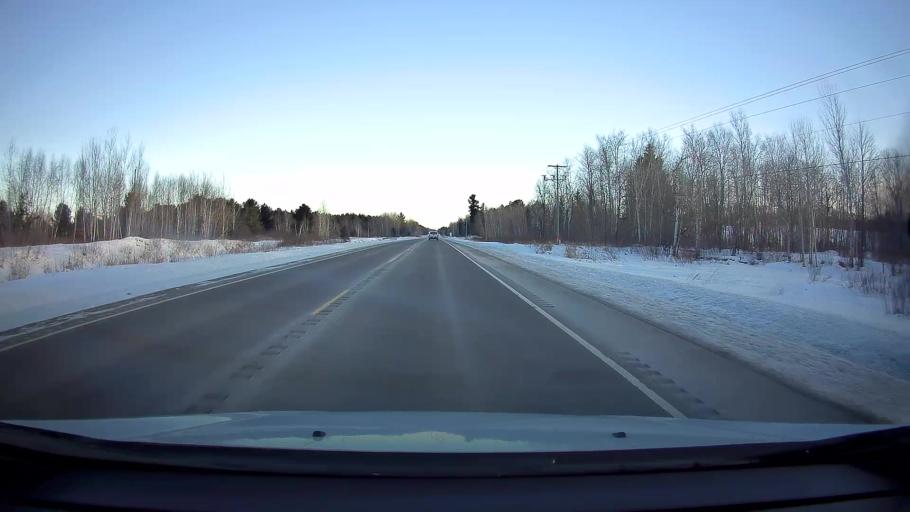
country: US
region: Wisconsin
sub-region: Washburn County
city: Shell Lake
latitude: 45.7161
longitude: -91.9405
